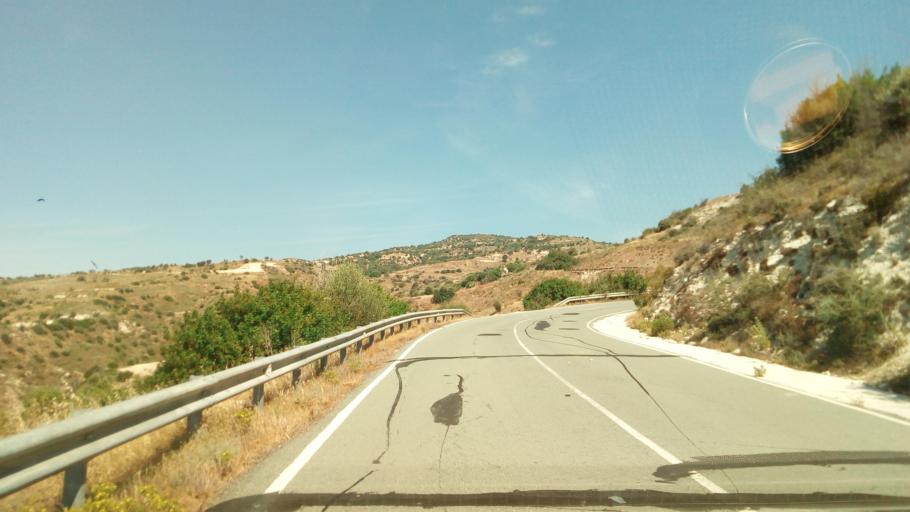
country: CY
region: Limassol
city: Pachna
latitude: 34.7946
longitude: 32.6905
